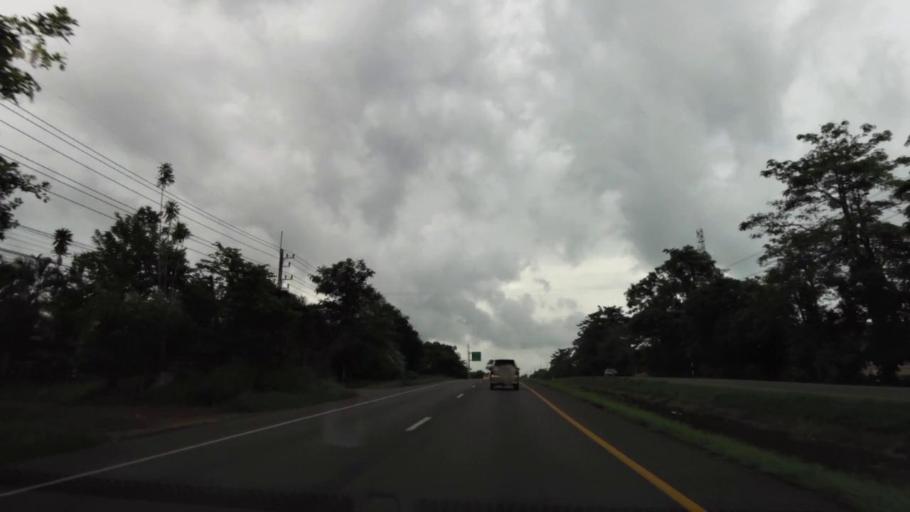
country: TH
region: Chanthaburi
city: Tha Mai
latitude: 12.6854
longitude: 102.0017
